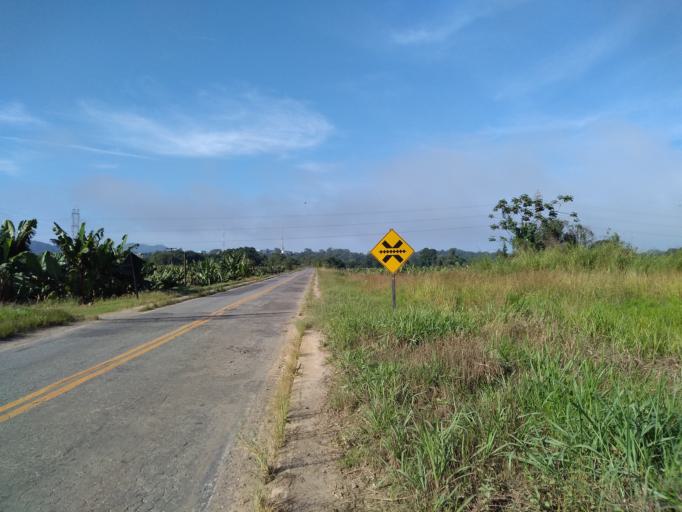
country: BR
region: Sao Paulo
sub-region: Jacupiranga
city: Jacupiranga
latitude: -24.6874
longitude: -48.0094
